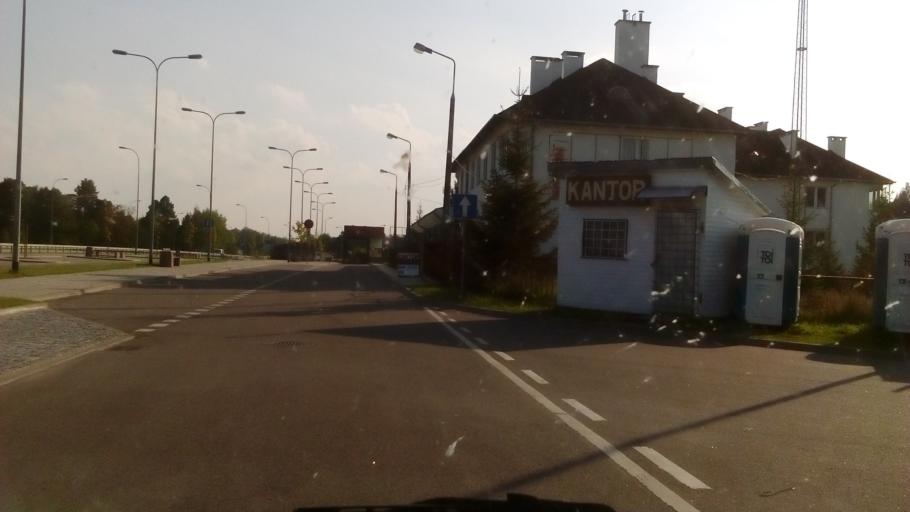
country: LT
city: Lazdijai
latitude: 54.1612
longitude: 23.4738
